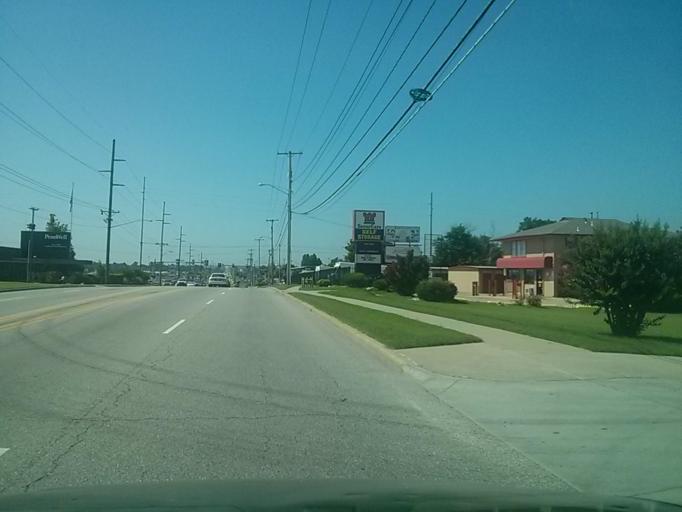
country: US
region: Oklahoma
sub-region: Tulsa County
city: Tulsa
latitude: 36.1424
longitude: -95.9046
